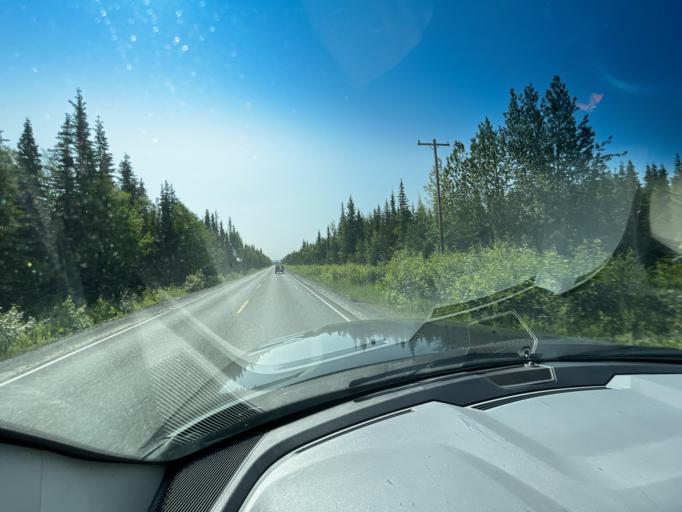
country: US
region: Alaska
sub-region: Kenai Peninsula Borough
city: Cohoe
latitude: 60.3113
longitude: -151.2922
